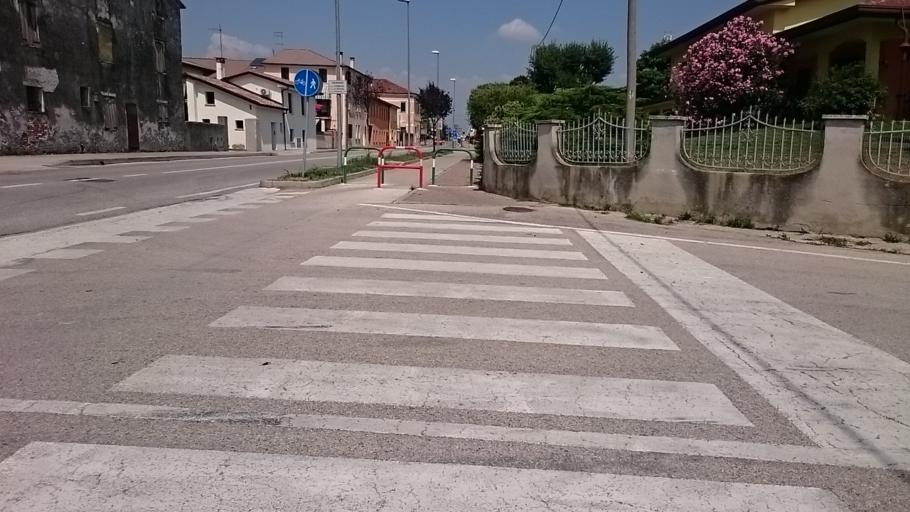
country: IT
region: Veneto
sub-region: Provincia di Padova
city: Cittadella
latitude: 45.6286
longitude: 11.7918
